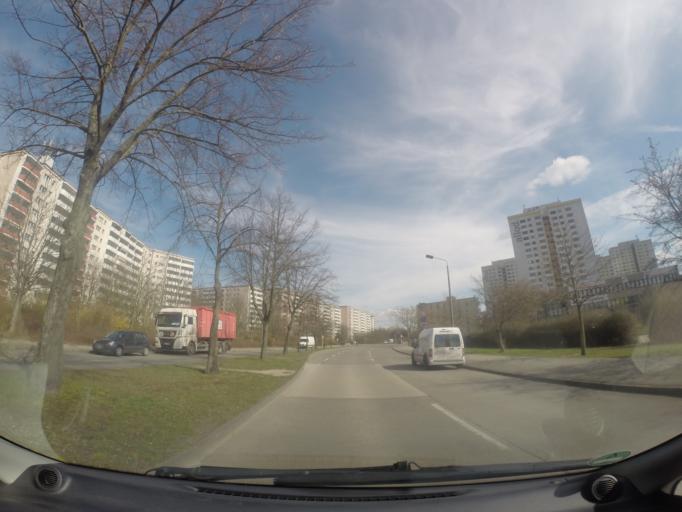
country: DE
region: Berlin
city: Marzahn
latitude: 52.5563
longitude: 13.5619
